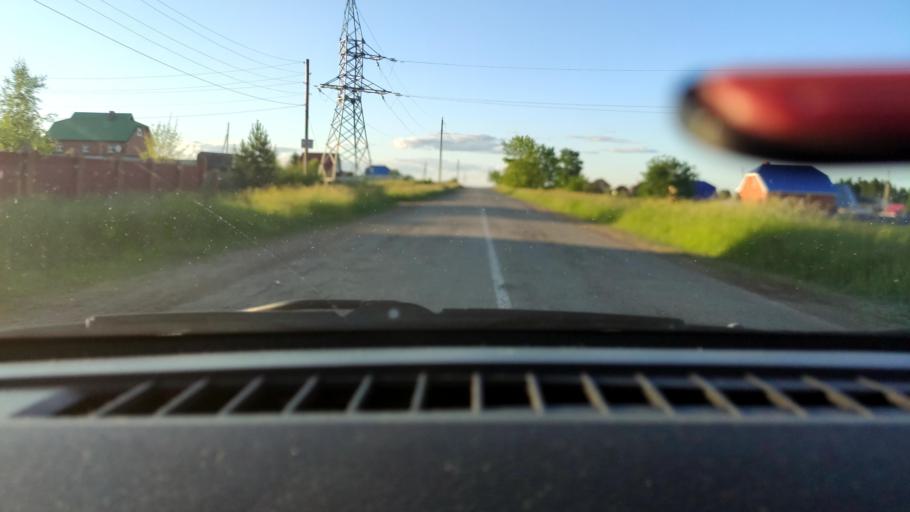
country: RU
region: Perm
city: Kultayevo
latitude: 57.9308
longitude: 55.8627
